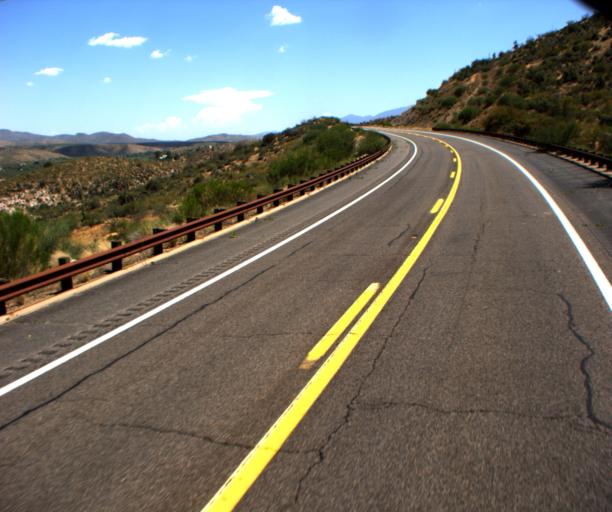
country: US
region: Arizona
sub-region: Gila County
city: Claypool
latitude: 33.5089
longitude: -110.8690
